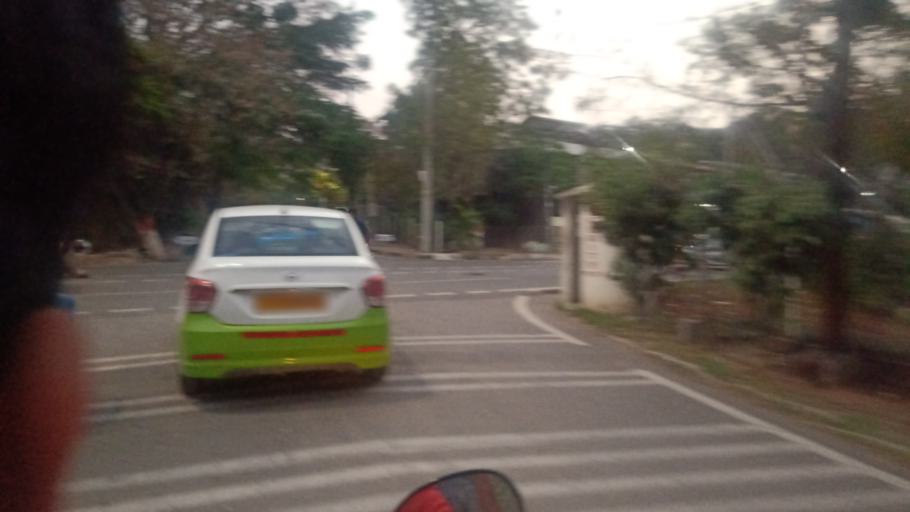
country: IN
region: Telangana
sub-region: Rangareddi
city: Kukatpalli
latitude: 17.4997
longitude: 78.3984
